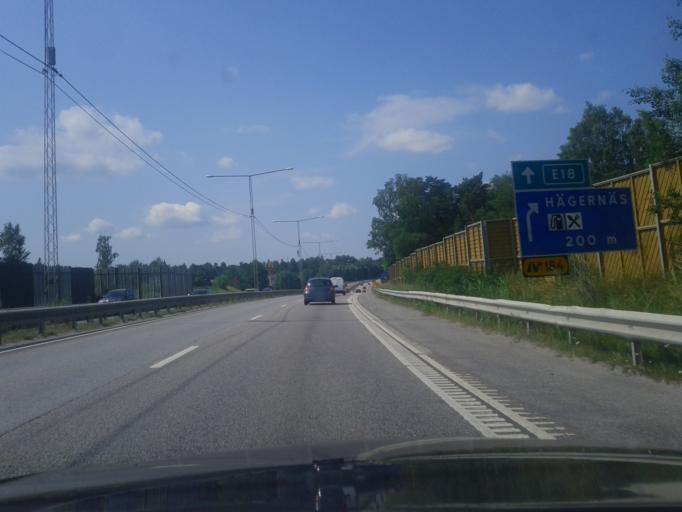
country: SE
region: Stockholm
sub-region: Taby Kommun
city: Taby
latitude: 59.4471
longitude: 18.1253
